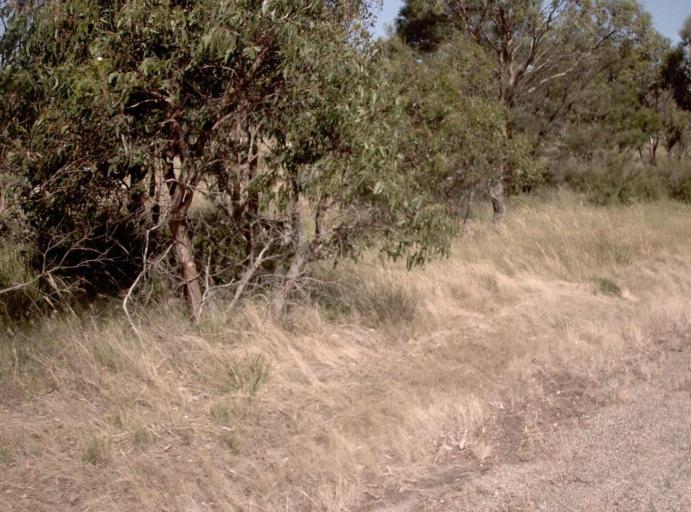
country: AU
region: Victoria
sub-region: Wellington
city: Sale
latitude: -38.2781
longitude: 147.1511
